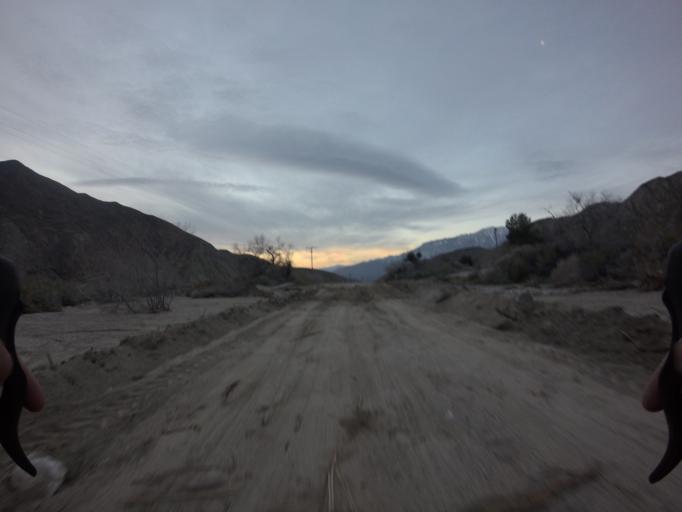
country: US
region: California
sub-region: San Bernardino County
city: Morongo Valley
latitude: 33.9791
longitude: -116.6532
